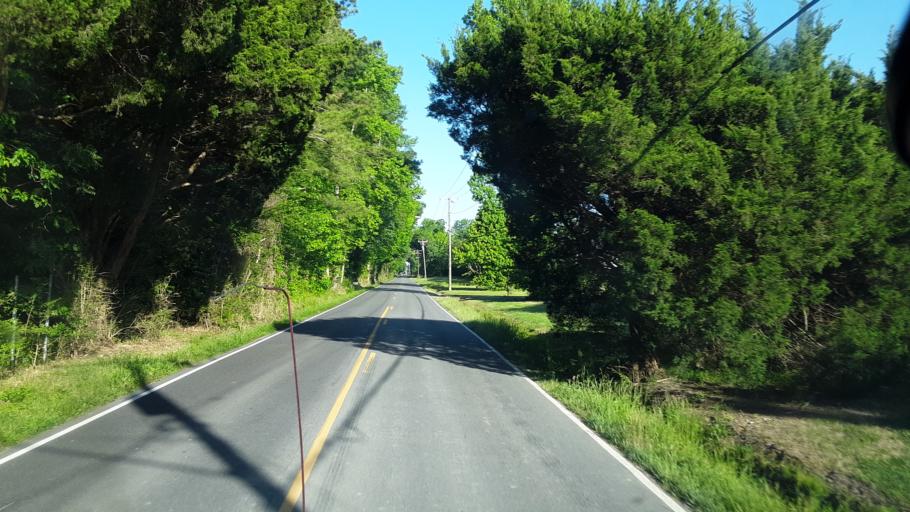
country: US
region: Virginia
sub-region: City of Virginia Beach
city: Virginia Beach
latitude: 36.7242
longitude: -76.0679
